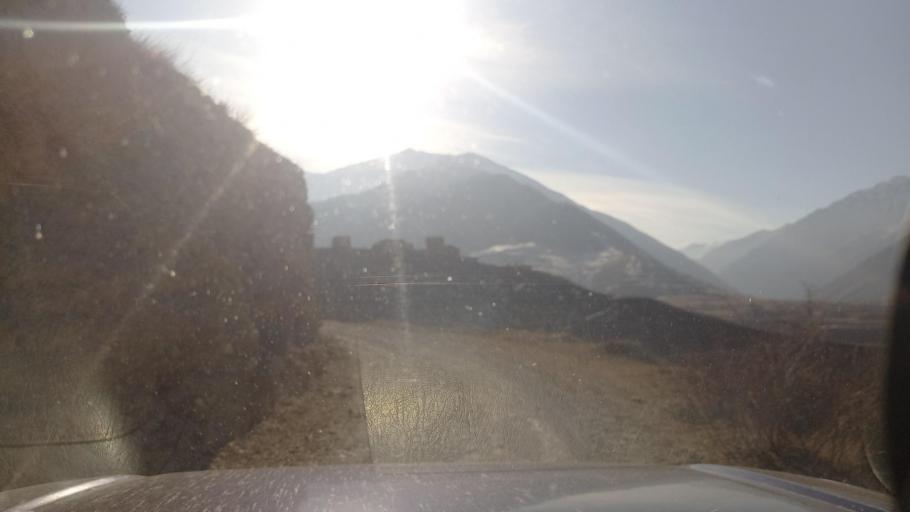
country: RU
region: Ingushetiya
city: Dzhayrakh
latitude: 42.8458
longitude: 44.6589
